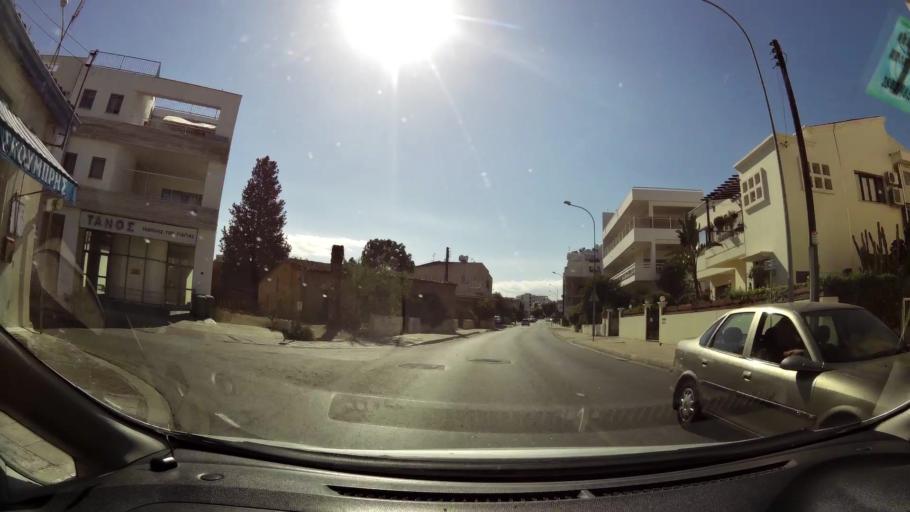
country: CY
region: Lefkosia
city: Nicosia
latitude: 35.1434
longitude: 33.3440
